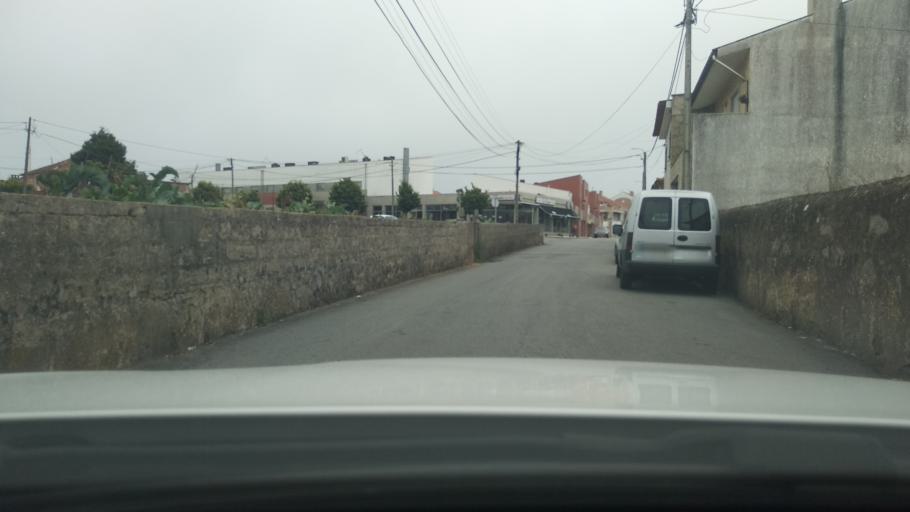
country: PT
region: Aveiro
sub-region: Espinho
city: Silvalde
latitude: 40.9949
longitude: -8.6280
